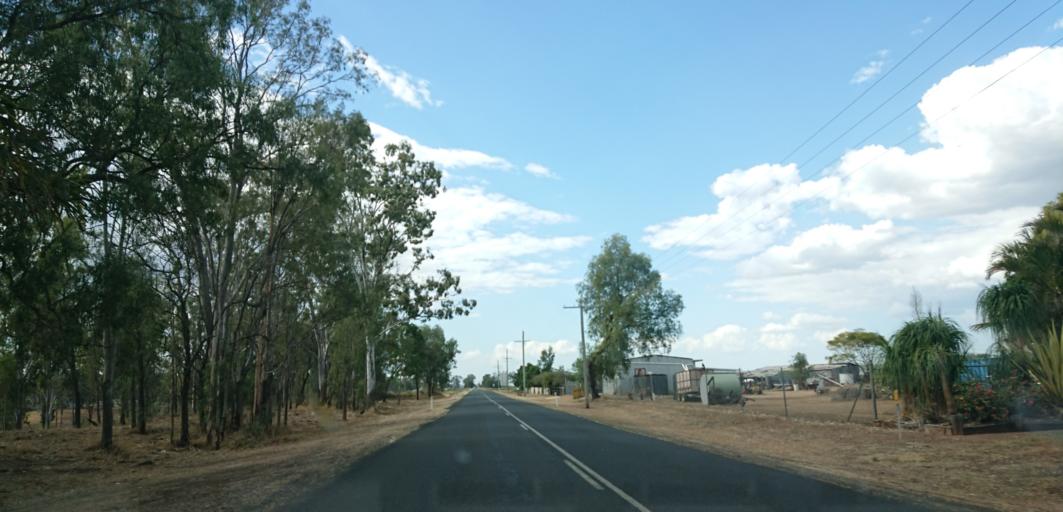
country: AU
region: Queensland
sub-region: Lockyer Valley
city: Gatton
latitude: -27.6067
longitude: 152.2104
